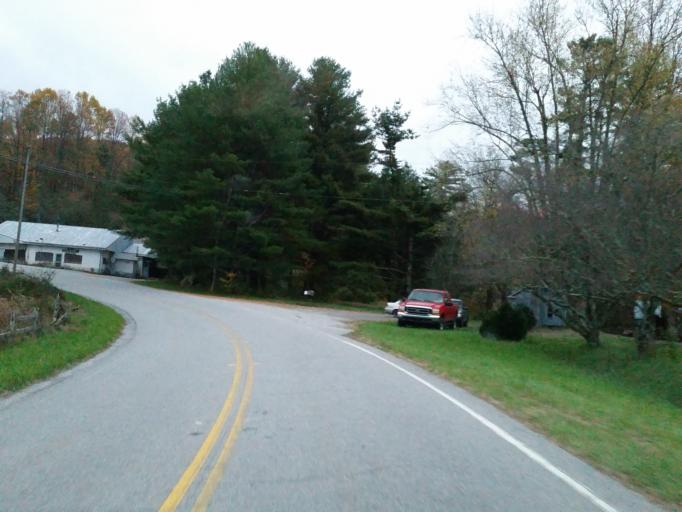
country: US
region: Georgia
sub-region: Lumpkin County
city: Dahlonega
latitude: 34.6836
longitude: -84.0188
